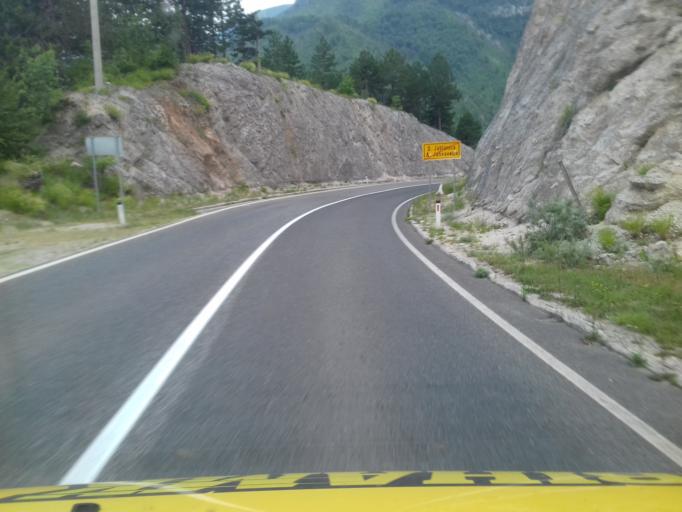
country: BA
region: Federation of Bosnia and Herzegovina
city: Jablanica
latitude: 43.6291
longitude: 17.7536
